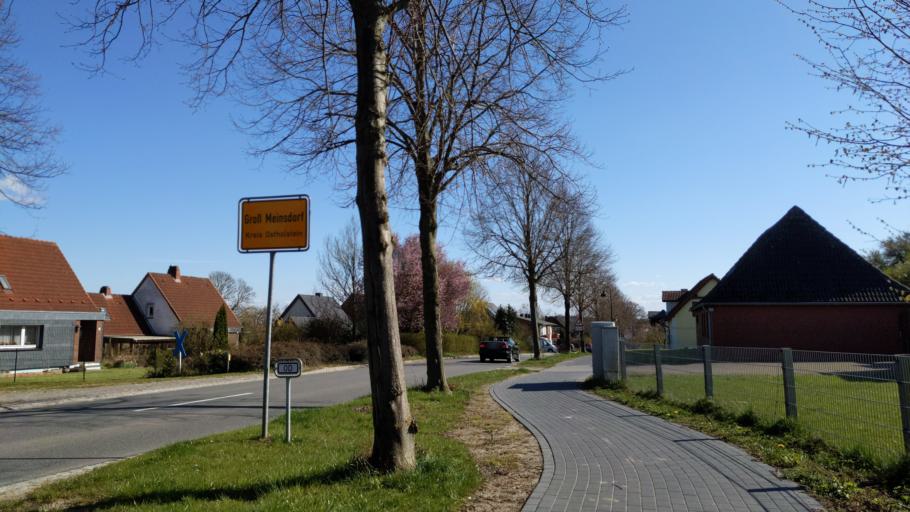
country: DE
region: Schleswig-Holstein
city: Eutin
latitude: 54.1101
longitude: 10.6108
